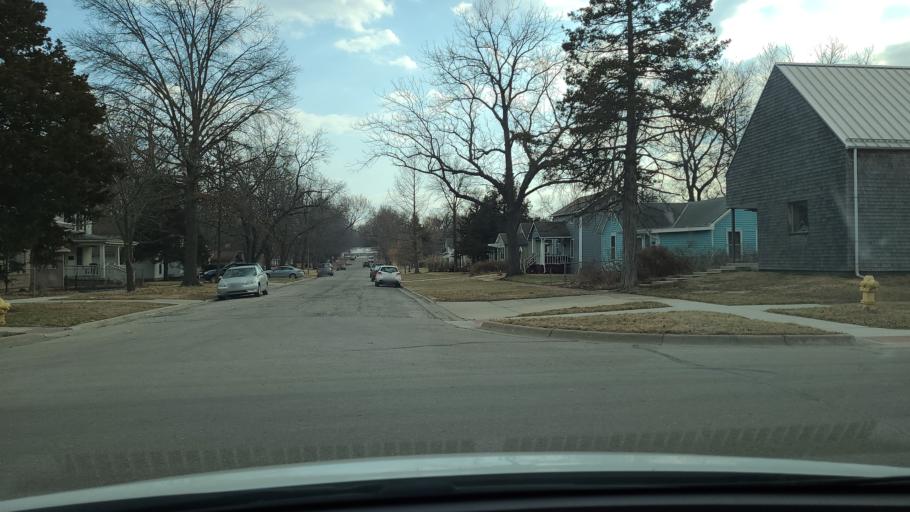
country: US
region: Kansas
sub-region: Douglas County
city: Lawrence
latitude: 38.9598
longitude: -95.2312
